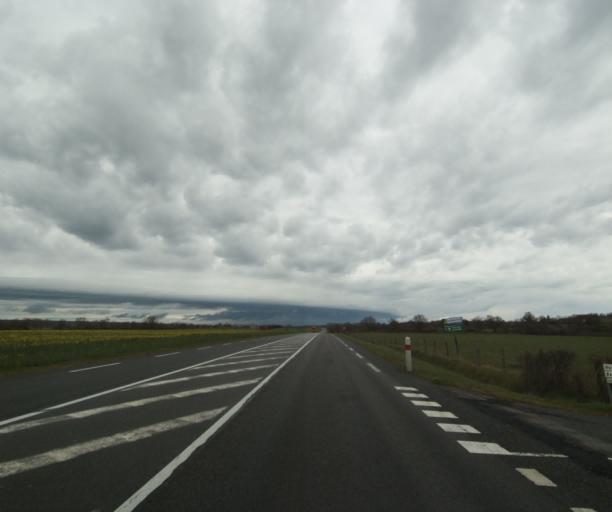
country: FR
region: Auvergne
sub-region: Departement de l'Allier
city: Bessay-sur-Allier
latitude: 46.4775
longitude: 3.3670
